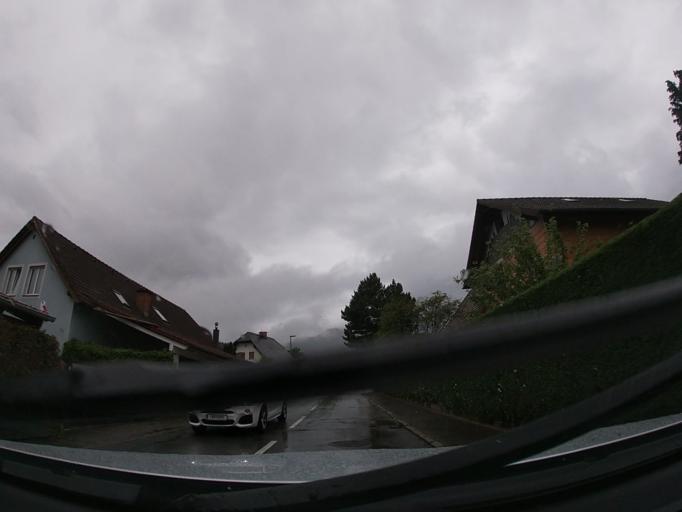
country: AT
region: Styria
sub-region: Politischer Bezirk Leoben
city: Trofaiach
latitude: 47.4251
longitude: 14.9881
